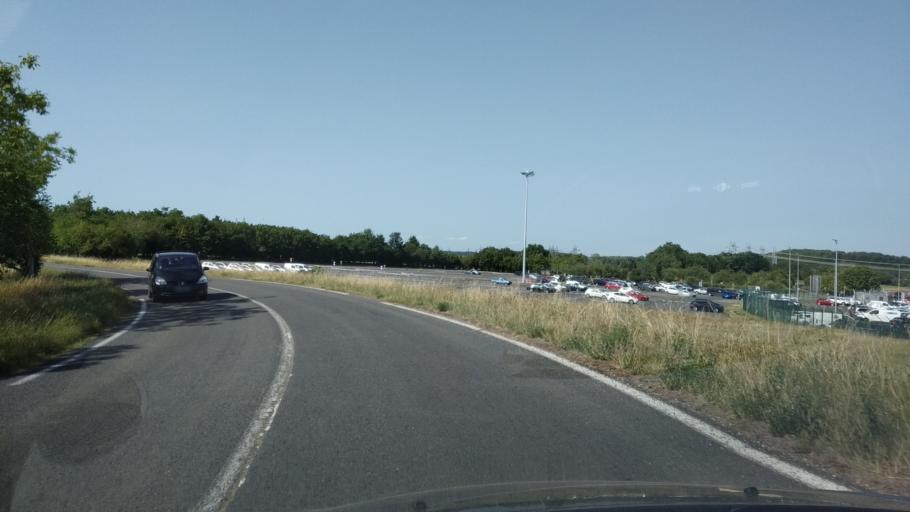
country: FR
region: Poitou-Charentes
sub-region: Departement de la Vienne
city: Lussac-les-Chateaux
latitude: 46.4598
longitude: 0.6467
